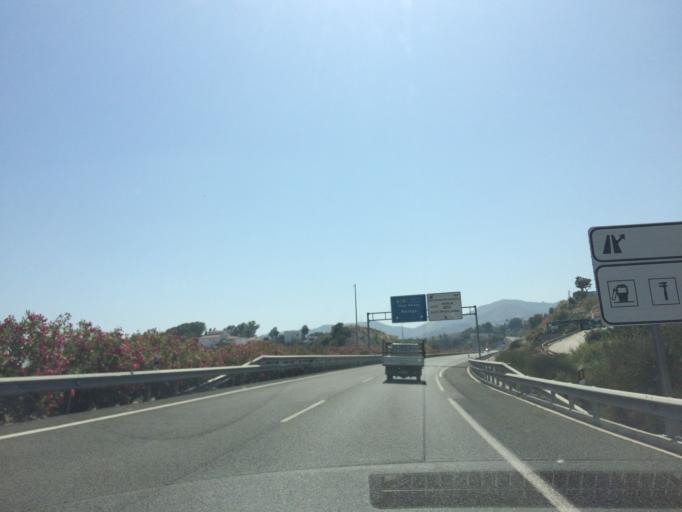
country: ES
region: Andalusia
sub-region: Provincia de Malaga
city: Nerja
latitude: 36.7642
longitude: -3.8809
